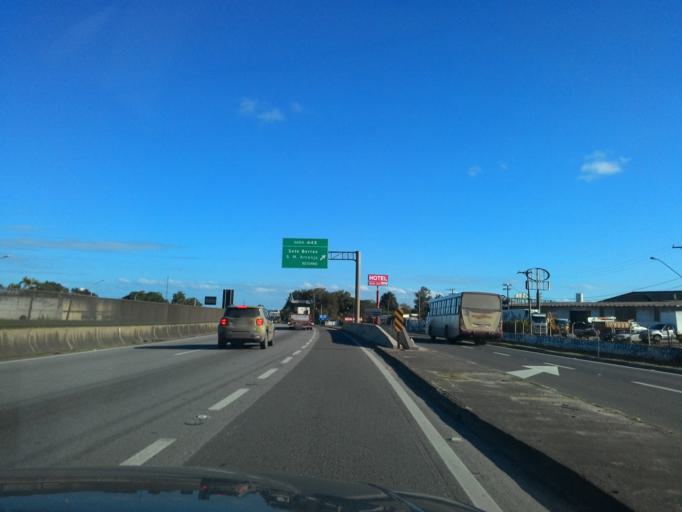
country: BR
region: Sao Paulo
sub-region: Registro
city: Registro
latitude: -24.5025
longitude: -47.8472
